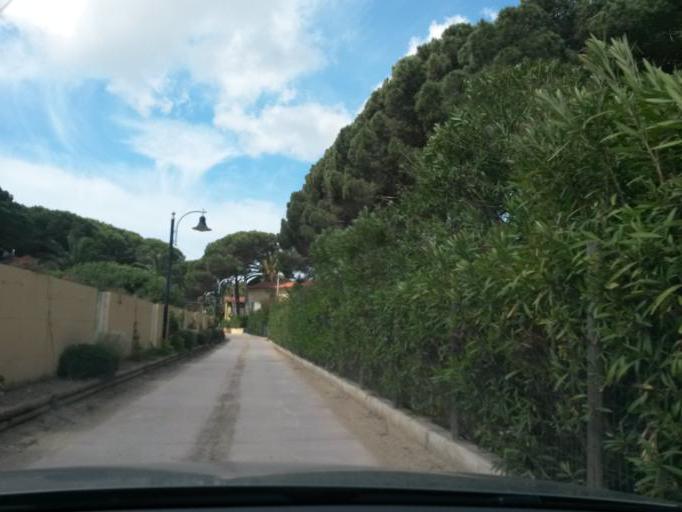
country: IT
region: Tuscany
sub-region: Provincia di Livorno
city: Porto Azzurro
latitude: 42.7558
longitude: 10.4024
